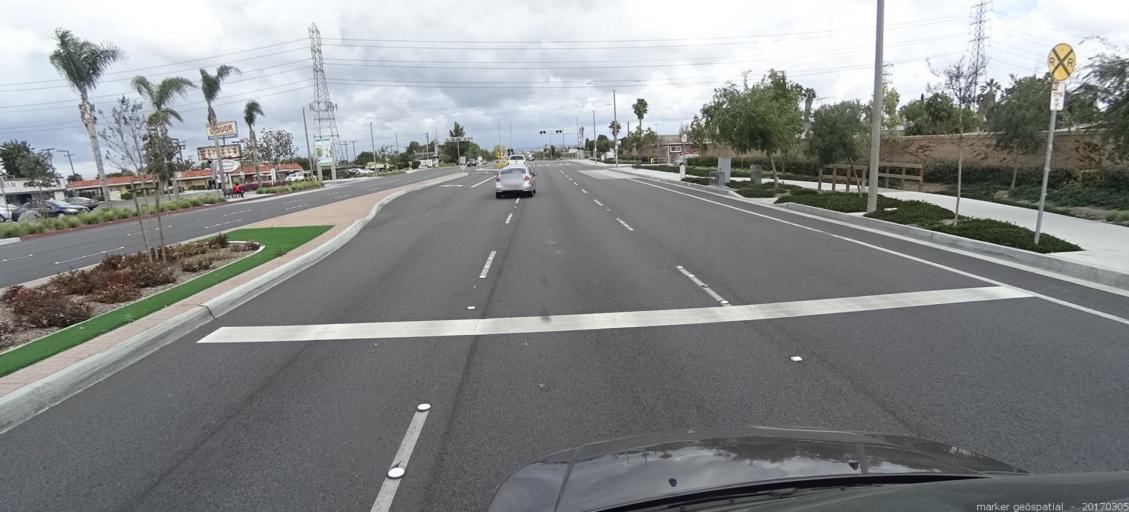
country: US
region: California
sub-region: Orange County
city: Stanton
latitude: 33.8055
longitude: -117.9588
